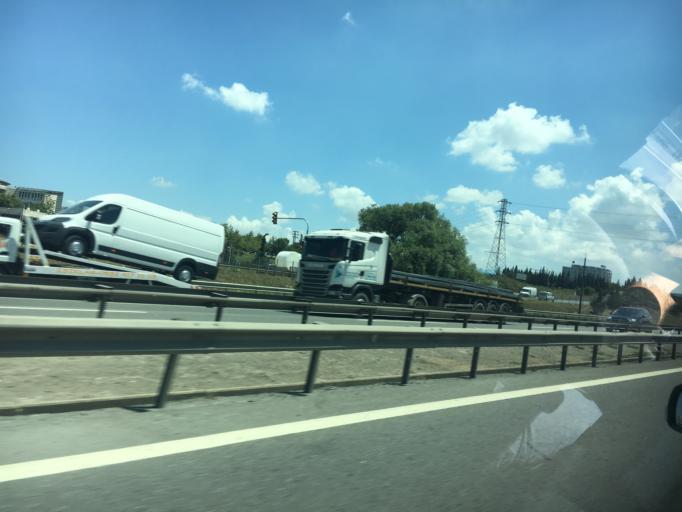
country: TR
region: Kocaeli
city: Balcik
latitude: 40.8899
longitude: 29.3726
